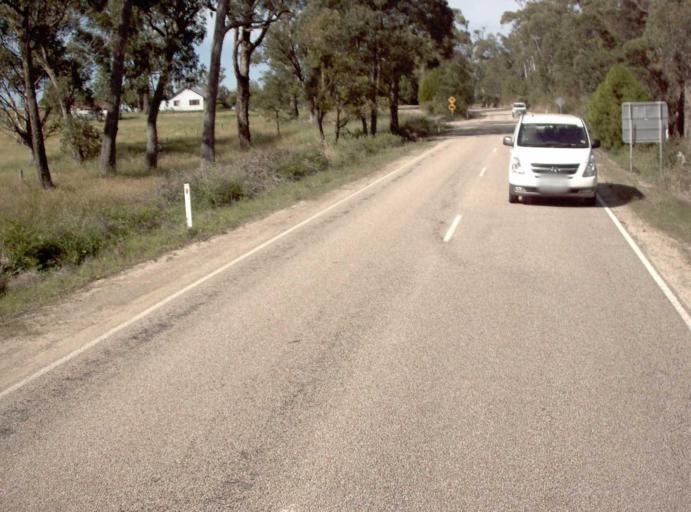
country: AU
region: Victoria
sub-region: East Gippsland
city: Lakes Entrance
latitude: -37.5281
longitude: 148.1562
